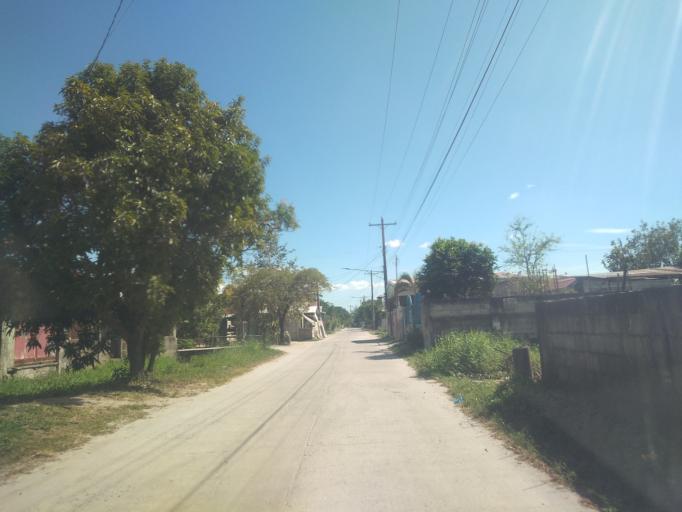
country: PH
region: Central Luzon
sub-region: Province of Pampanga
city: Bacolor
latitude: 15.0130
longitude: 120.6430
